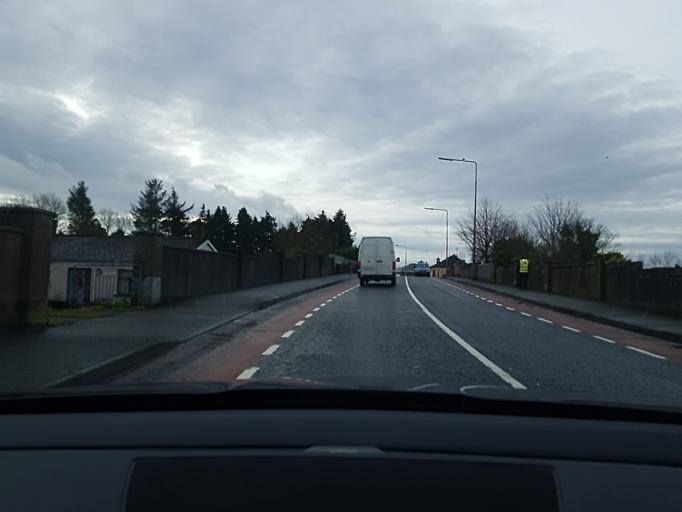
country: IE
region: Connaught
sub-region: Maigh Eo
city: Castlebar
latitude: 53.8480
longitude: -9.2887
